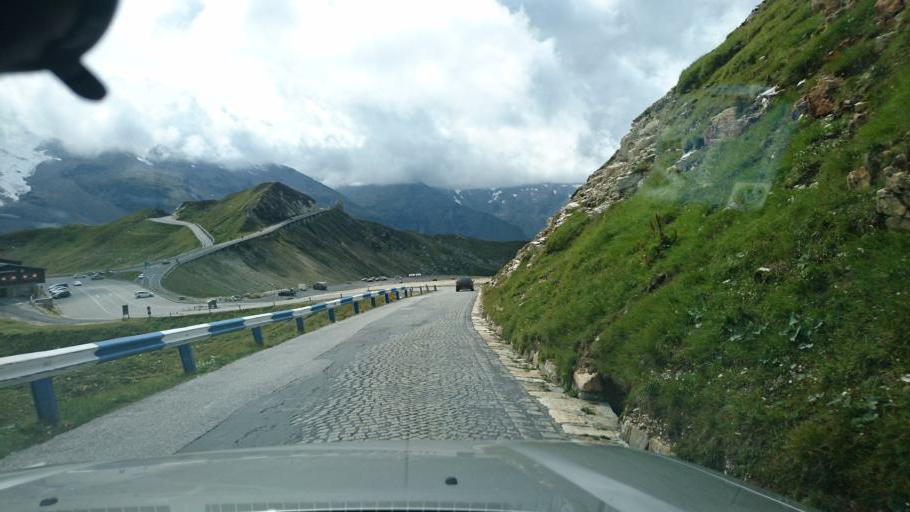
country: AT
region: Carinthia
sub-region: Politischer Bezirk Spittal an der Drau
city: Heiligenblut
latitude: 47.1195
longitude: 12.8306
